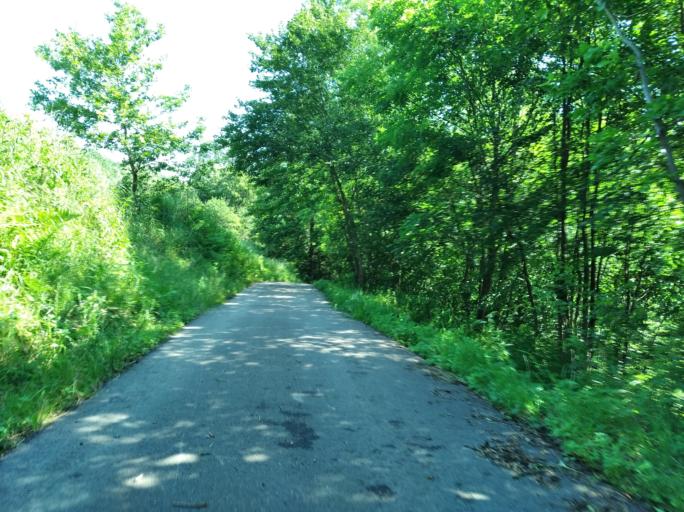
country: PL
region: Subcarpathian Voivodeship
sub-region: Powiat strzyzowski
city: Jawornik
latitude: 49.8232
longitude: 21.8435
